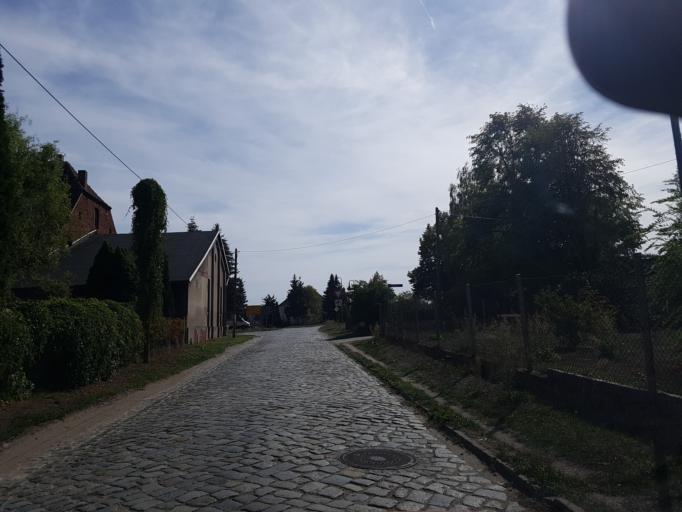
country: DE
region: Saxony-Anhalt
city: Lindau
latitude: 52.0277
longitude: 12.2251
